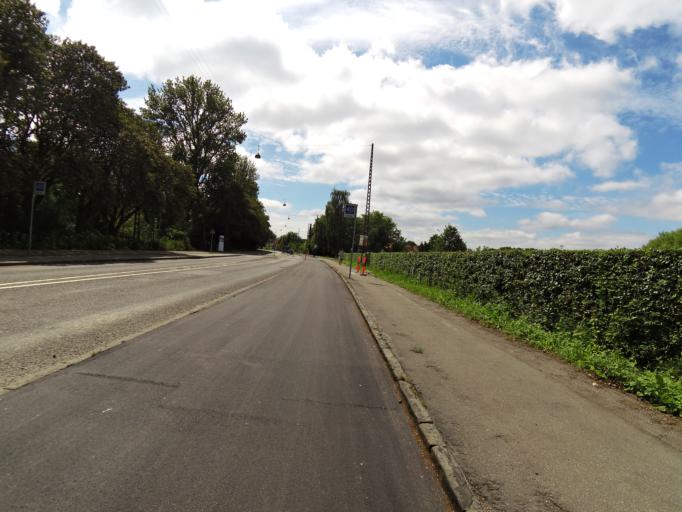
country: DK
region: Capital Region
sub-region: Frederiksberg Kommune
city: Frederiksberg
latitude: 55.7171
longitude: 12.5221
